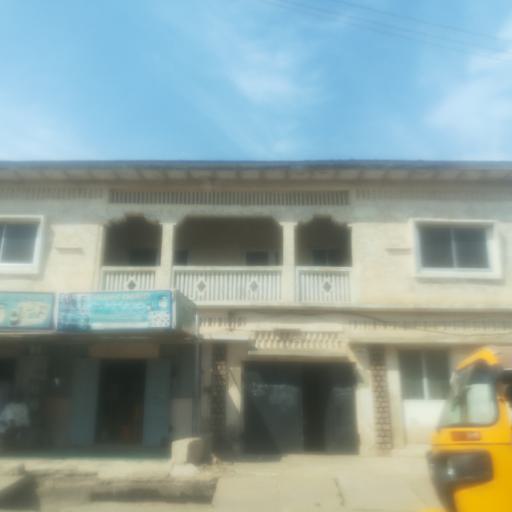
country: NG
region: Kano
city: Kano
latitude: 12.0149
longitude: 8.5104
